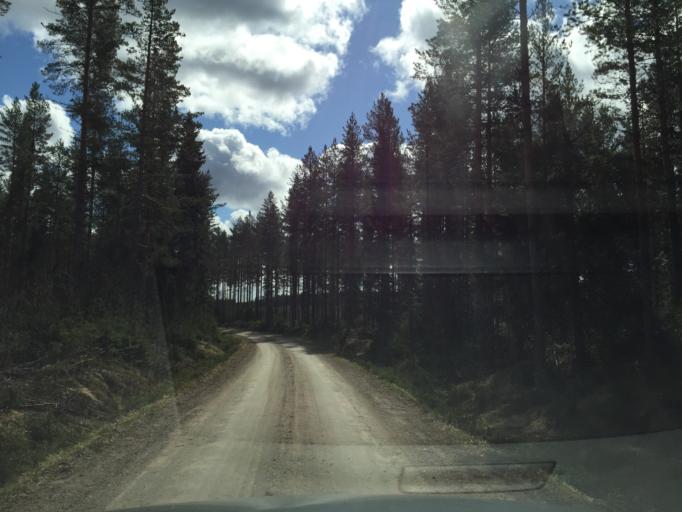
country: SE
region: Gaevleborg
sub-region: Bollnas Kommun
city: Arbra
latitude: 61.5239
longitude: 16.2854
